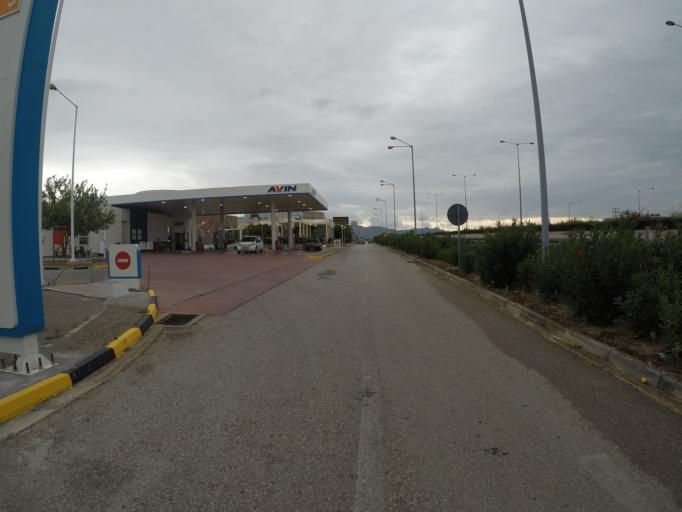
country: GR
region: Attica
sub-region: Nomarchia Dytikis Attikis
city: Megara
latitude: 37.9953
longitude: 23.3652
